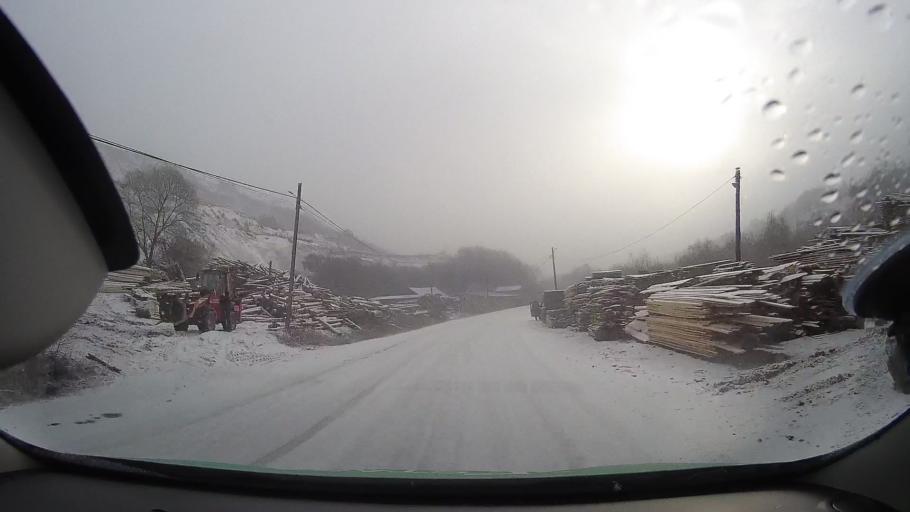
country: RO
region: Alba
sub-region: Comuna Livezile
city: Livezile
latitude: 46.3612
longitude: 23.6112
